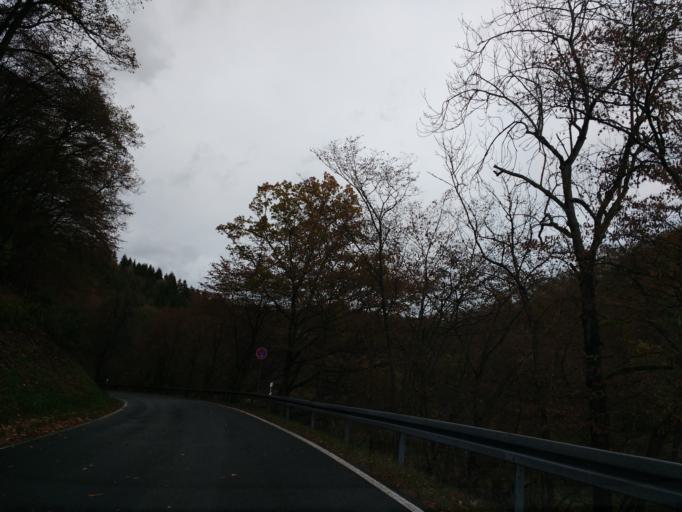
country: DE
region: Hesse
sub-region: Regierungsbezirk Kassel
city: Vohl
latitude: 51.1855
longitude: 8.9480
